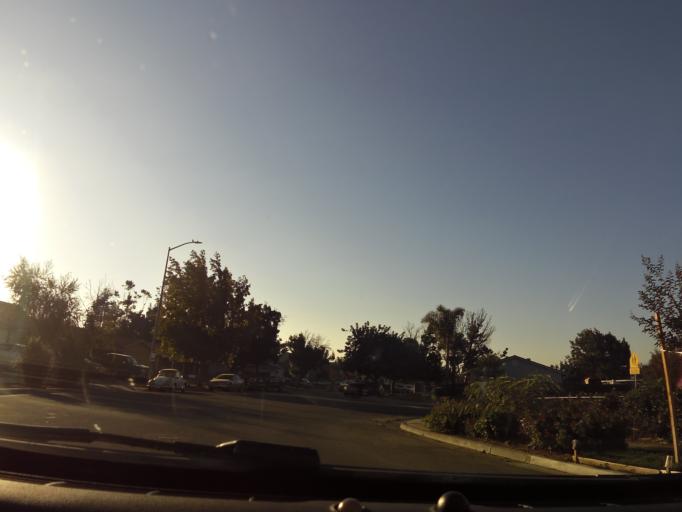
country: US
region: California
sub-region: San Benito County
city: Hollister
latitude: 36.8559
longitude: -121.3944
